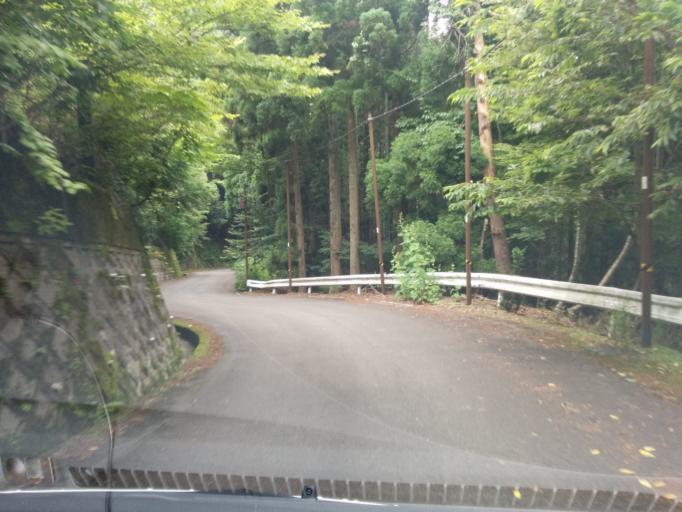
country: JP
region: Kyoto
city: Miyazu
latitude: 35.4547
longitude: 135.1153
